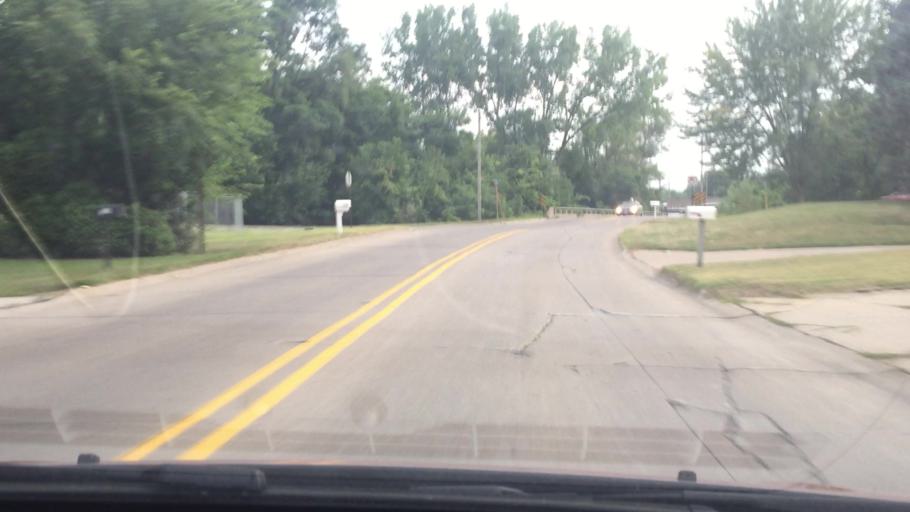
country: US
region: Iowa
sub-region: Muscatine County
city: Muscatine
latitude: 41.4457
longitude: -91.0392
